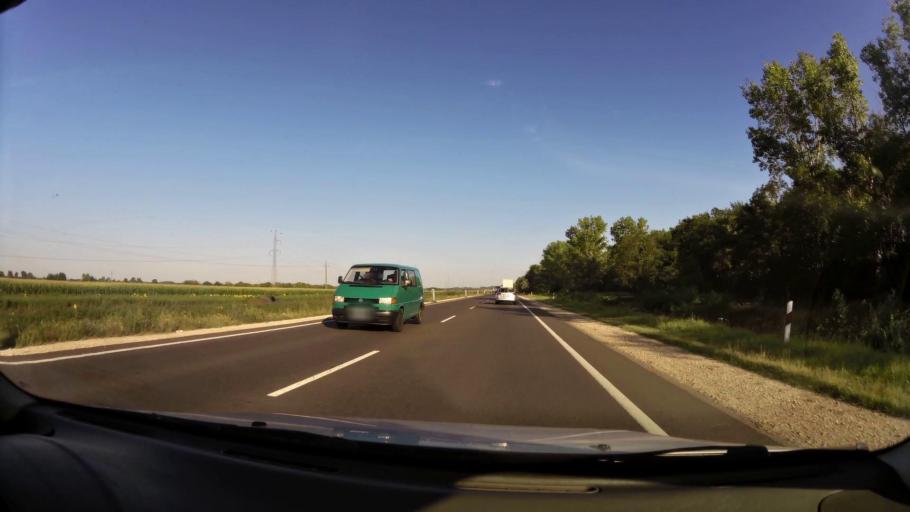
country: HU
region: Pest
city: Cegled
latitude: 47.2064
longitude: 19.7665
